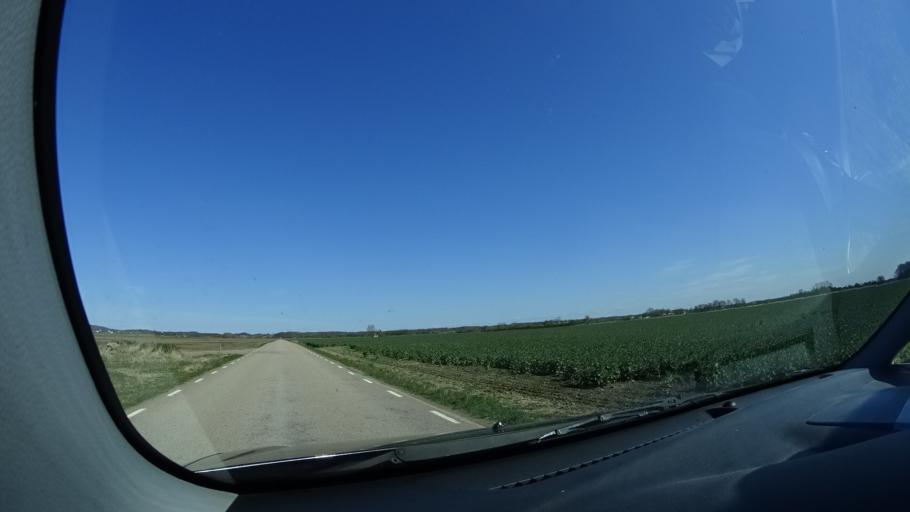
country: SE
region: Skane
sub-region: Hoganas Kommun
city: Hoganas
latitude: 56.2326
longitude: 12.5862
